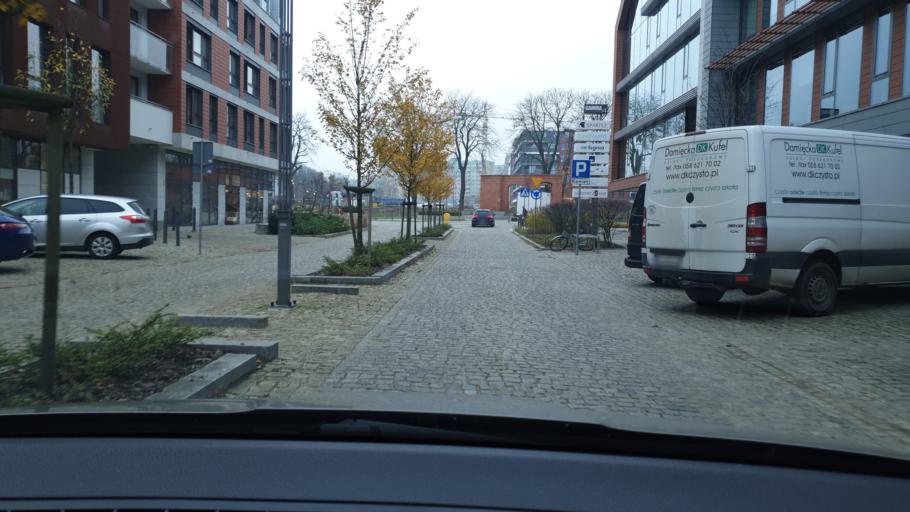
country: PL
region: Pomeranian Voivodeship
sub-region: Gdansk
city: Gdansk
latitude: 54.3838
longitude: 18.5921
